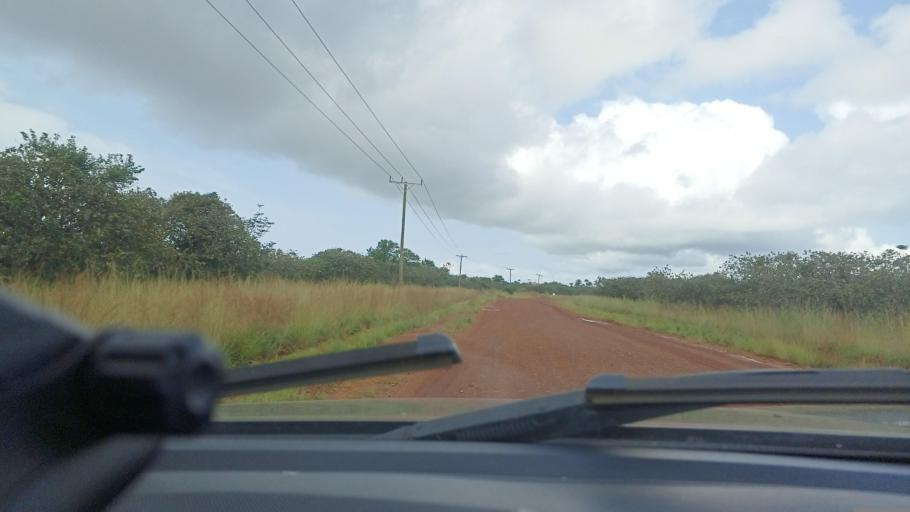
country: LR
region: Grand Cape Mount
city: Robertsport
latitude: 6.6921
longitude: -11.2790
